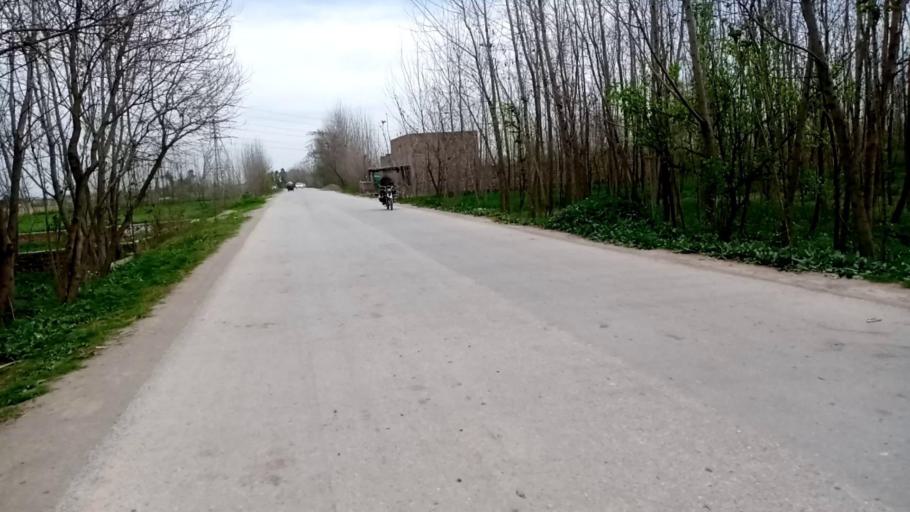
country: PK
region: Khyber Pakhtunkhwa
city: Charsadda
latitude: 34.0628
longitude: 71.6935
